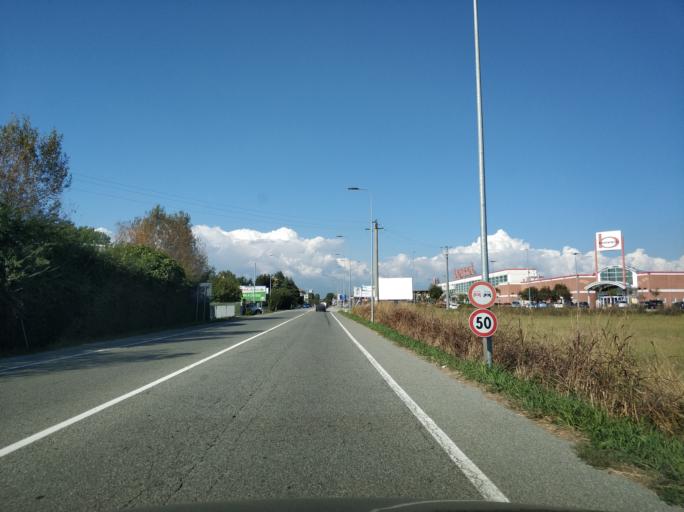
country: IT
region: Piedmont
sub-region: Provincia di Torino
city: Caselle Torinese
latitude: 45.1656
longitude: 7.6542
